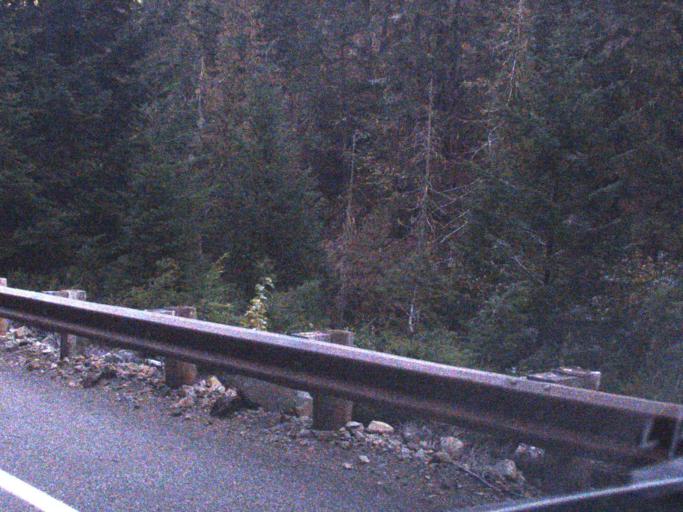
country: US
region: Washington
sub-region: Snohomish County
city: Darrington
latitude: 48.6766
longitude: -120.8805
